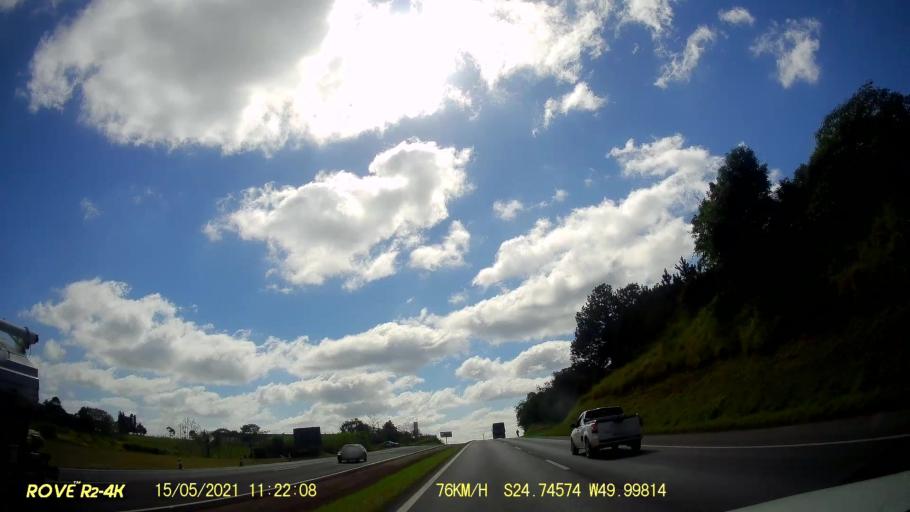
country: BR
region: Parana
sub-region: Castro
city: Castro
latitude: -24.7458
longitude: -49.9982
